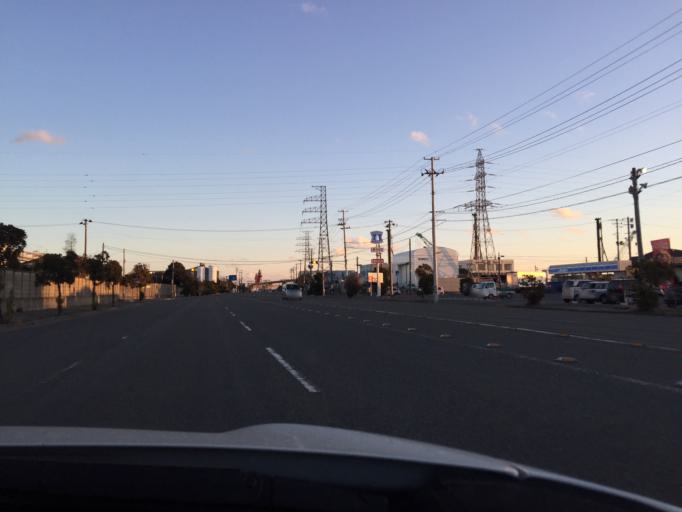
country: JP
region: Fukushima
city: Iwaki
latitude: 36.9420
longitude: 140.8758
